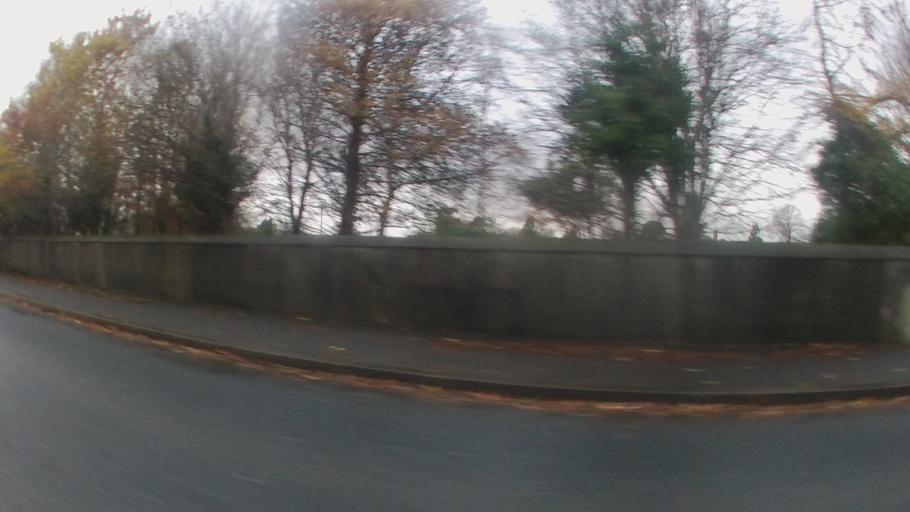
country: IE
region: Leinster
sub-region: Wicklow
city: Kilcoole
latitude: 53.1122
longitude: -6.0654
